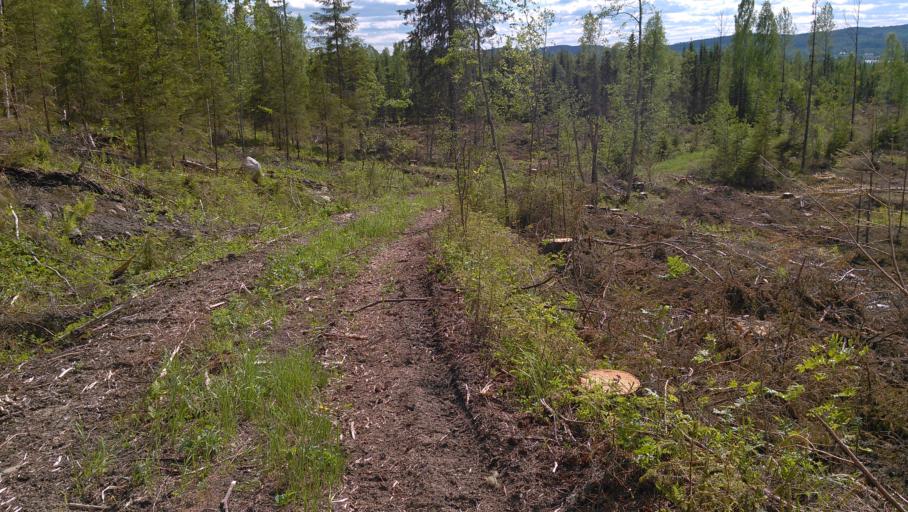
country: SE
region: Vaesterbotten
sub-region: Vannas Kommun
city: Vannasby
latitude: 63.9290
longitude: 19.8912
